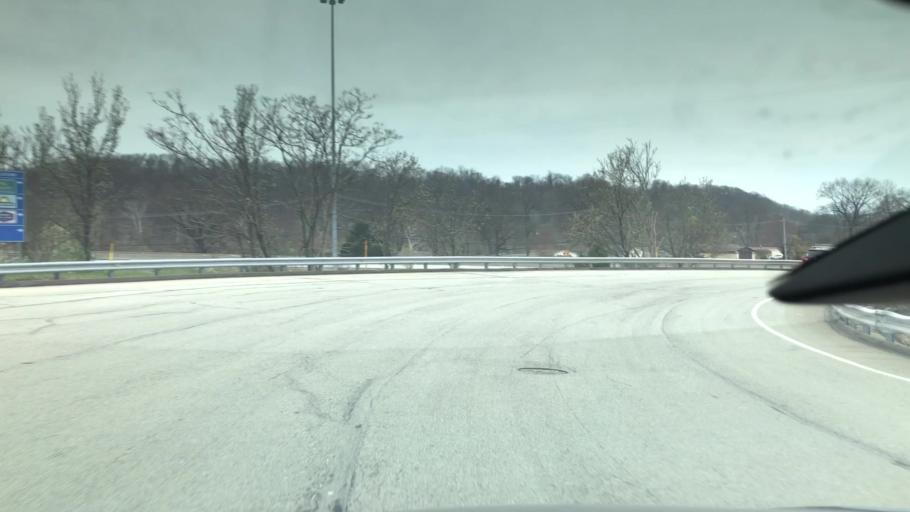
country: US
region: Pennsylvania
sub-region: Allegheny County
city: Oakmont
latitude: 40.5407
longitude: -79.8255
